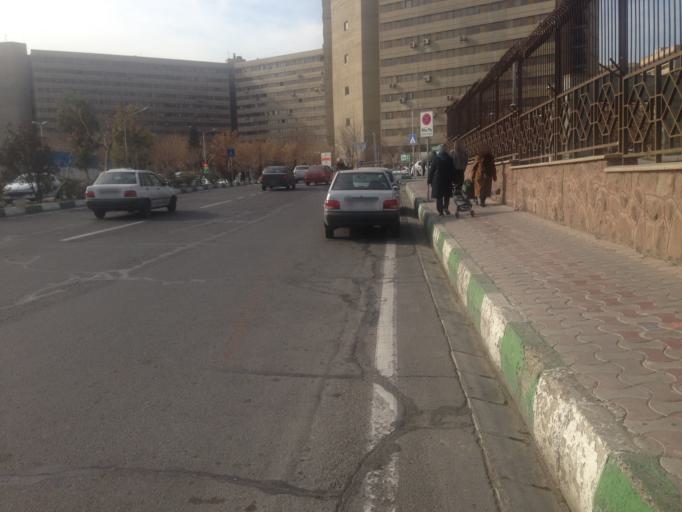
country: IR
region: Tehran
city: Tehran
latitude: 35.7119
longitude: 51.3075
